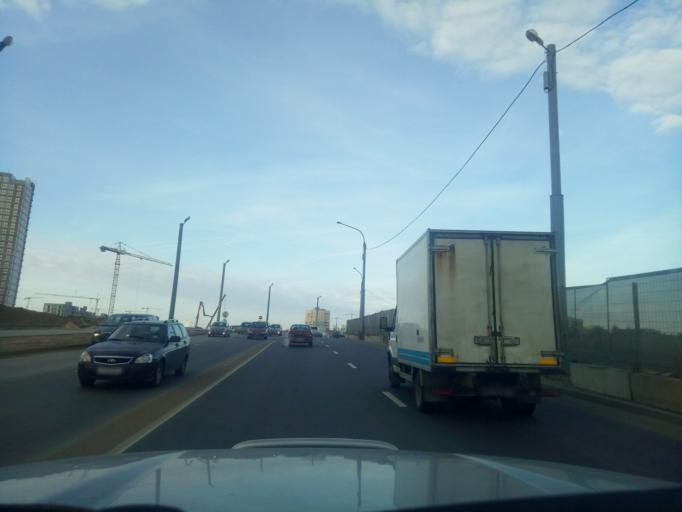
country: BY
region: Minsk
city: Minsk
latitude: 53.8717
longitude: 27.5475
